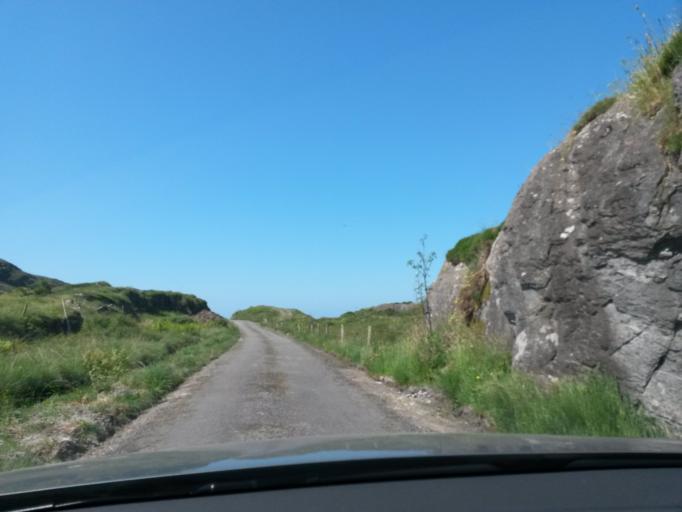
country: IE
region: Munster
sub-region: Ciarrai
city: Cahersiveen
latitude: 51.7319
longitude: -9.9671
